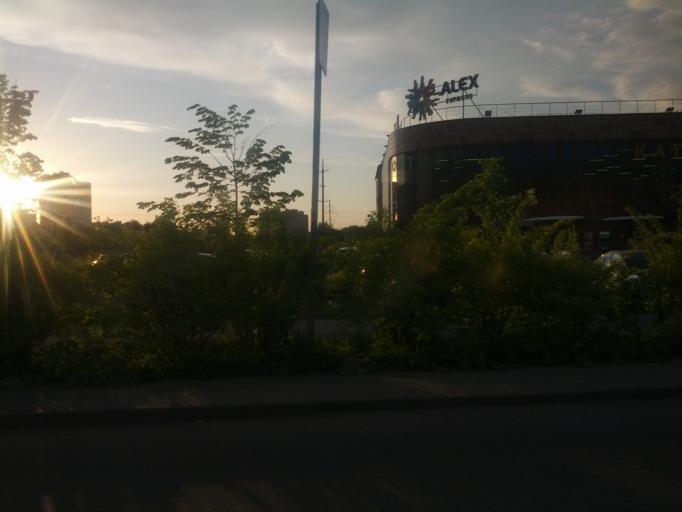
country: RU
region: St.-Petersburg
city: Krasnogvargeisky
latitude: 59.9118
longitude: 30.5041
